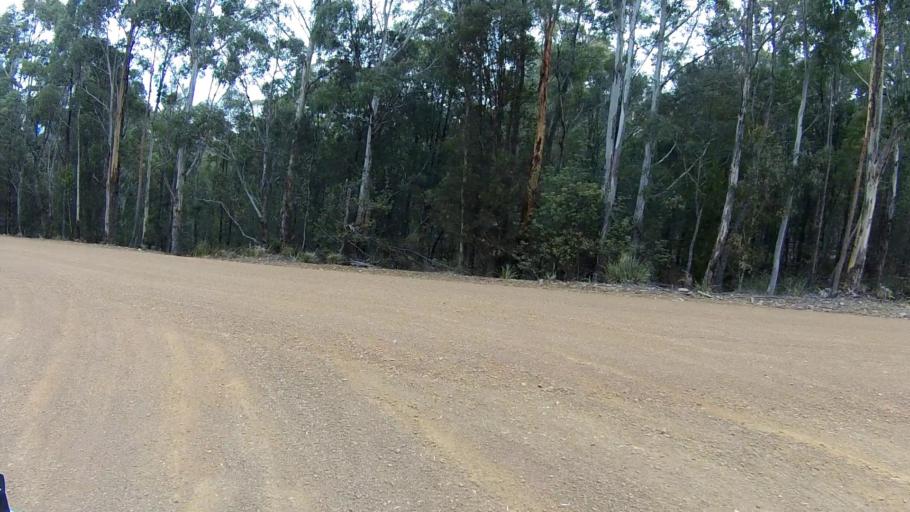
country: AU
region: Tasmania
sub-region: Sorell
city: Sorell
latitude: -42.6004
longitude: 147.8863
